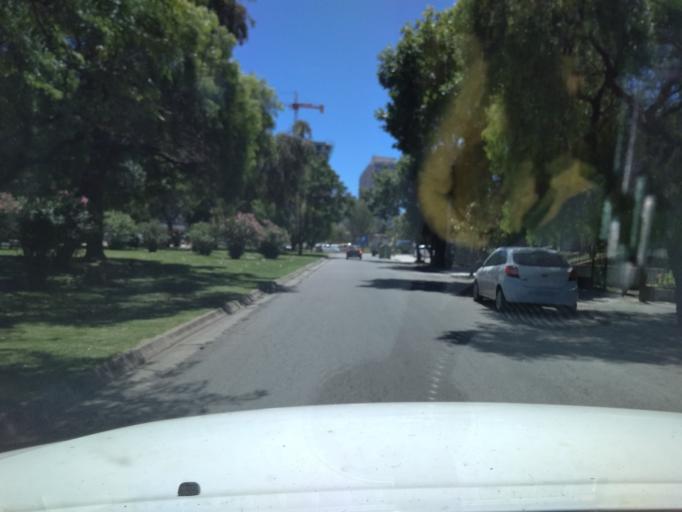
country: UY
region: Canelones
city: Paso de Carrasco
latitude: -34.8891
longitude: -56.1062
